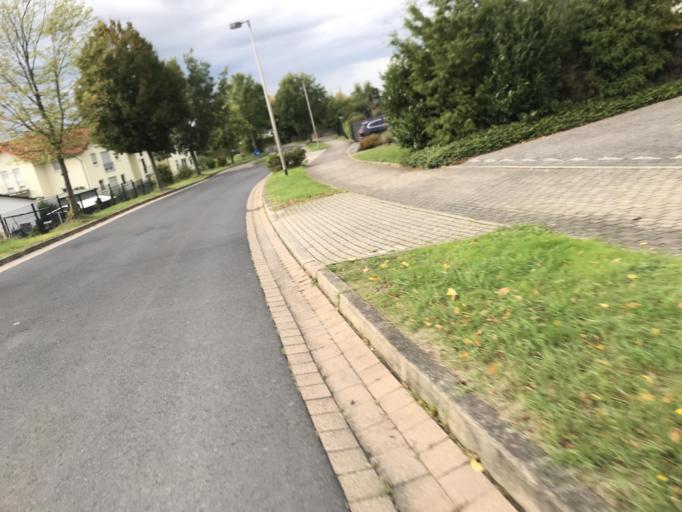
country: DE
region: Hesse
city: Borken
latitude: 51.0395
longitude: 9.2815
